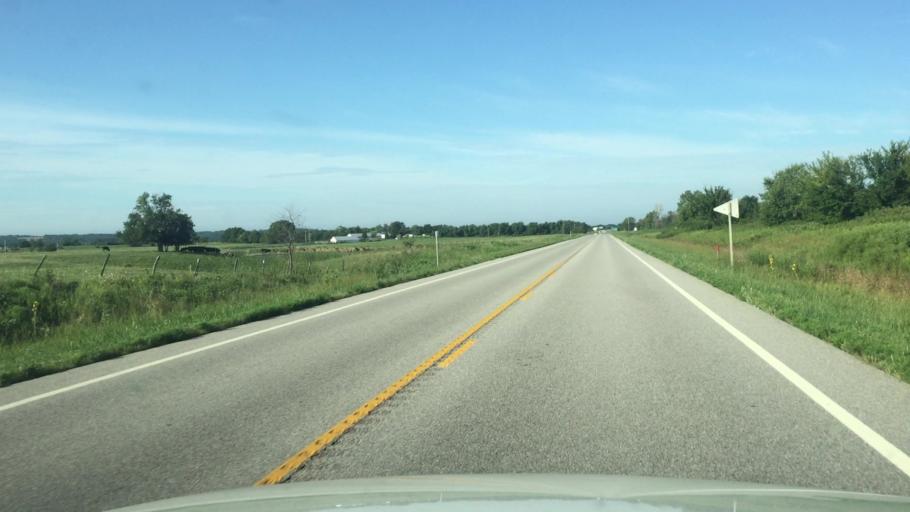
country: US
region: Kansas
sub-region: Anderson County
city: Garnett
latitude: 38.2934
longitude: -95.2005
